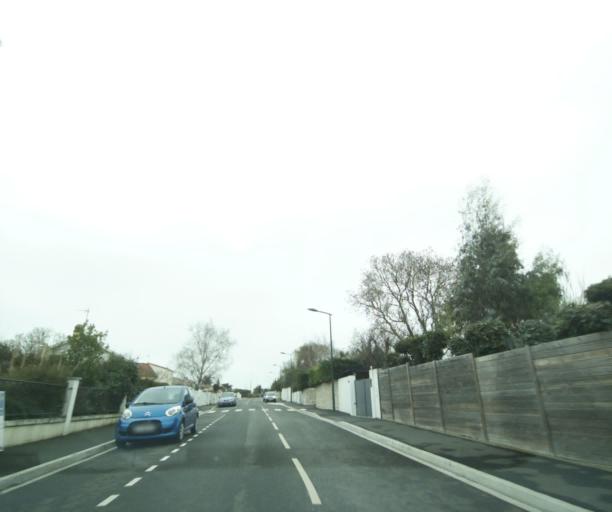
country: FR
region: Poitou-Charentes
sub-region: Departement de la Charente-Maritime
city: Lagord
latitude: 46.1834
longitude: -1.1432
